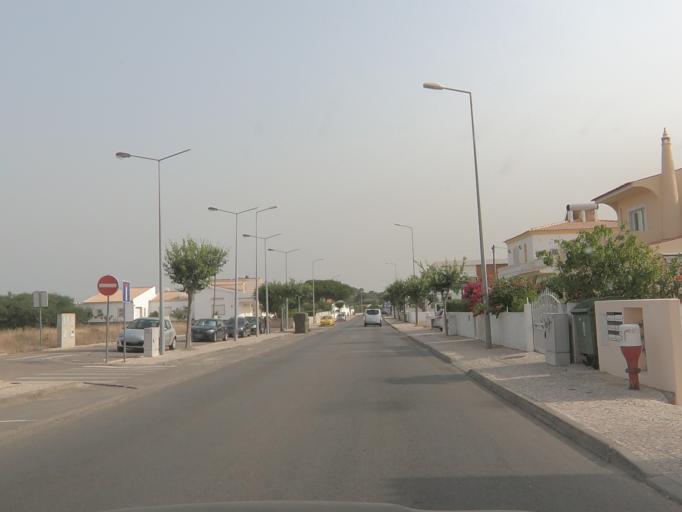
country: PT
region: Faro
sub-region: Albufeira
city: Guia
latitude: 37.0939
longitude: -8.3098
